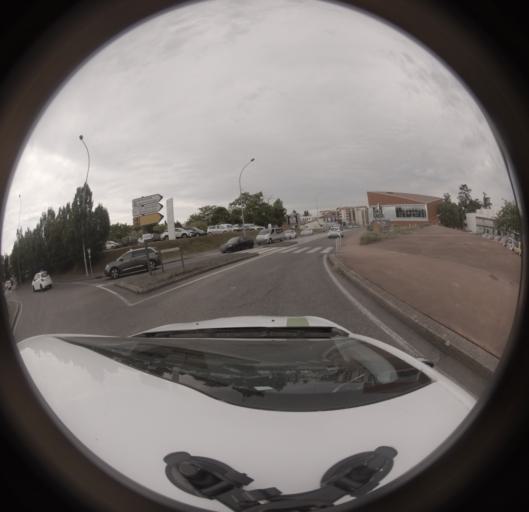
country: FR
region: Midi-Pyrenees
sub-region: Departement du Tarn-et-Garonne
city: Montauban
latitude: 44.0082
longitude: 1.3773
